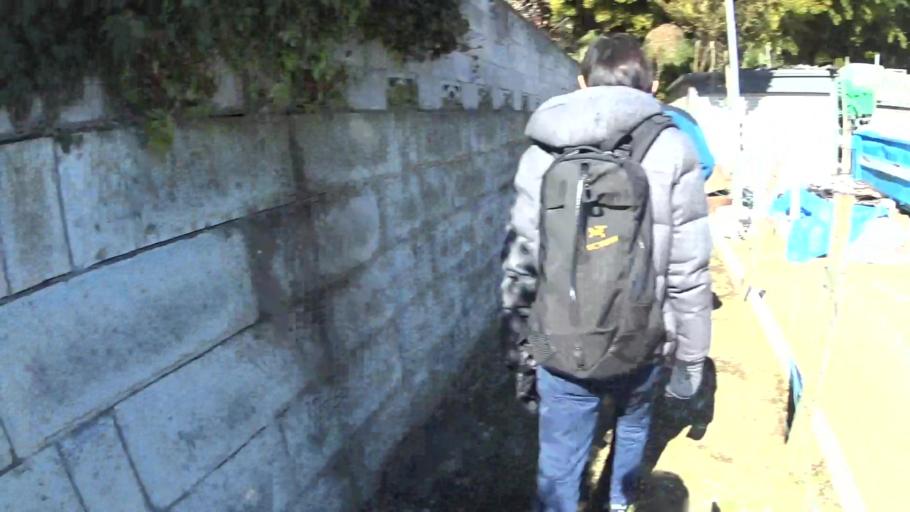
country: JP
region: Saitama
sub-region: Kawaguchi-shi
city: Hatogaya-honcho
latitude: 35.8512
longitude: 139.7552
